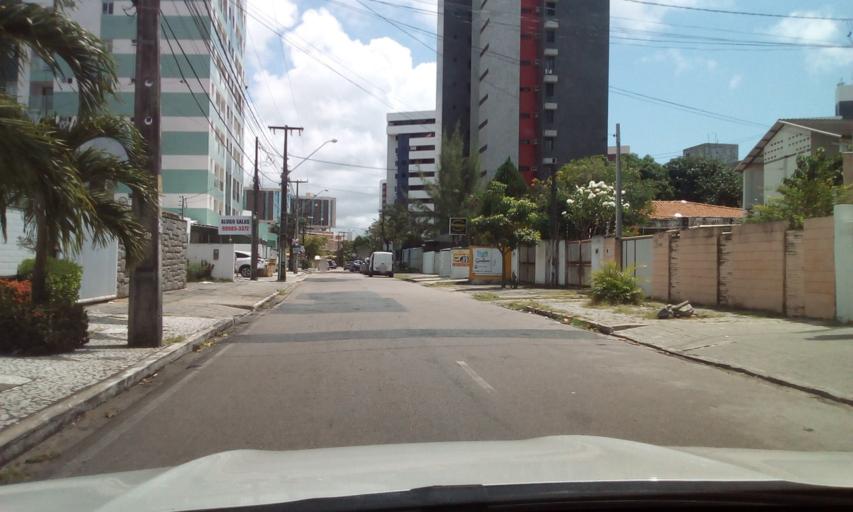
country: BR
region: Paraiba
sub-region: Joao Pessoa
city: Joao Pessoa
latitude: -7.0997
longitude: -34.8354
